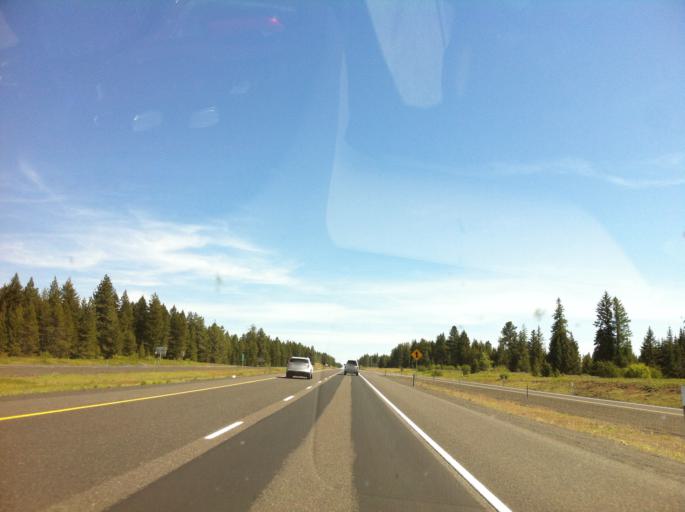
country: US
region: Oregon
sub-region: Umatilla County
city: Mission
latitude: 45.5067
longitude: -118.4264
